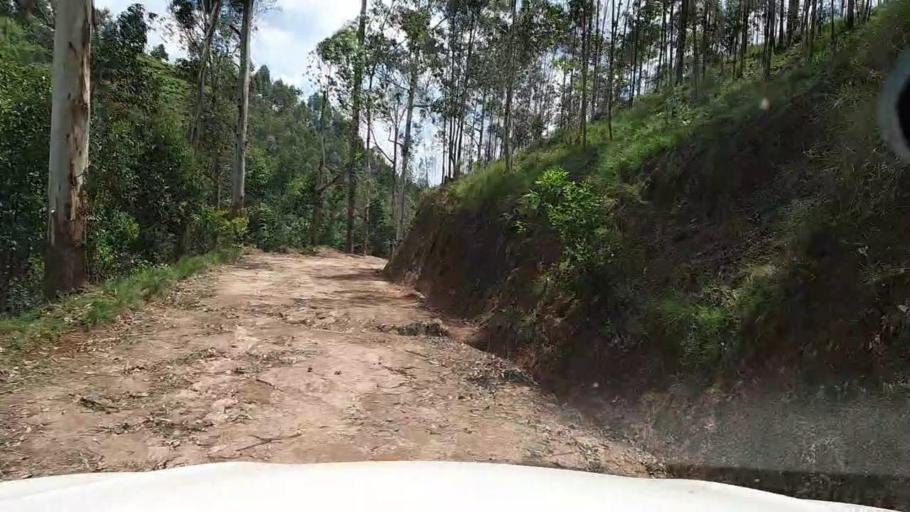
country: RW
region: Southern Province
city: Nzega
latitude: -2.6434
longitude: 29.4771
